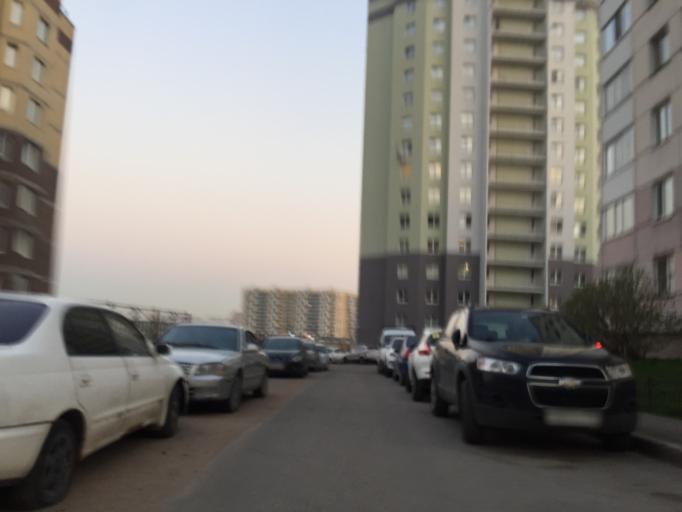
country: RU
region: Leningrad
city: Bugry
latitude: 60.0674
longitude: 30.4042
